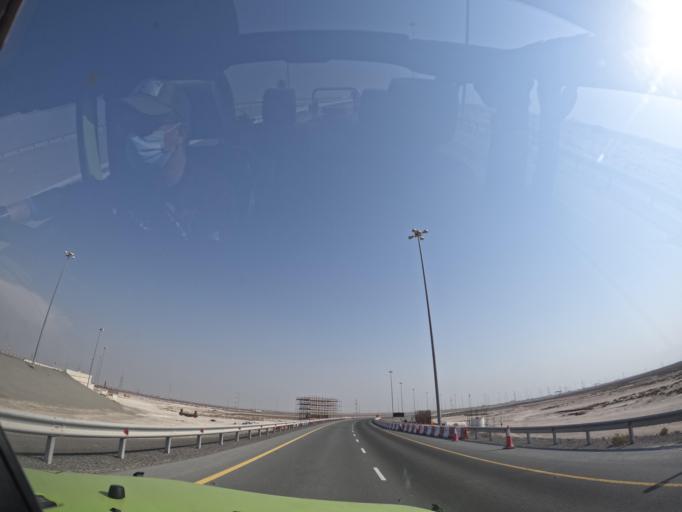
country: AE
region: Abu Dhabi
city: Abu Dhabi
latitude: 24.6776
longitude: 54.8111
